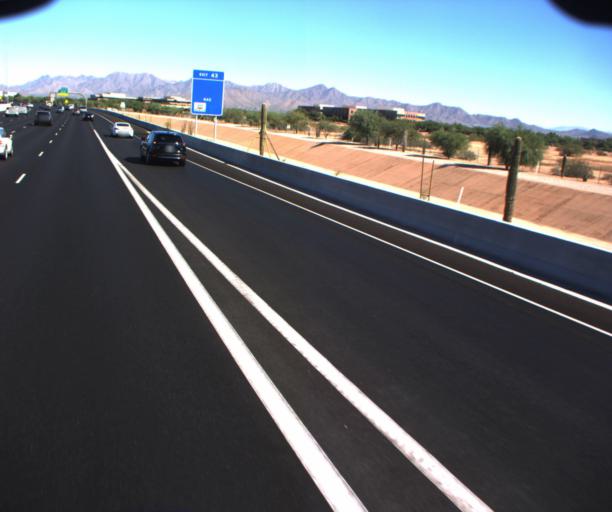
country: US
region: Arizona
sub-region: Maricopa County
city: Scottsdale
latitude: 33.5422
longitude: -111.8801
